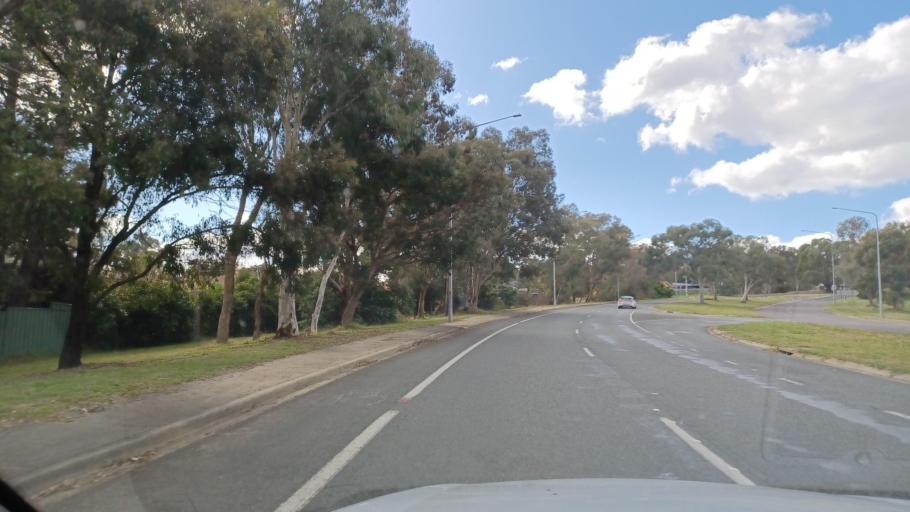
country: AU
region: Australian Capital Territory
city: Belconnen
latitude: -35.2080
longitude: 149.0474
